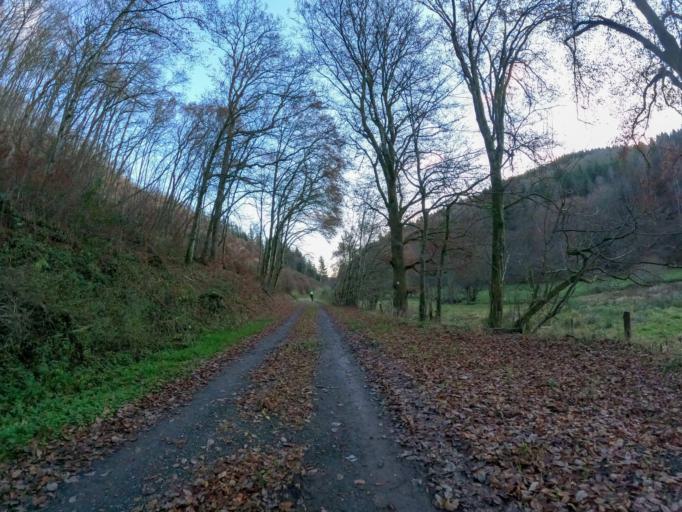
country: LU
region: Diekirch
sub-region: Canton de Wiltz
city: Bavigne
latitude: 49.9387
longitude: 5.8387
